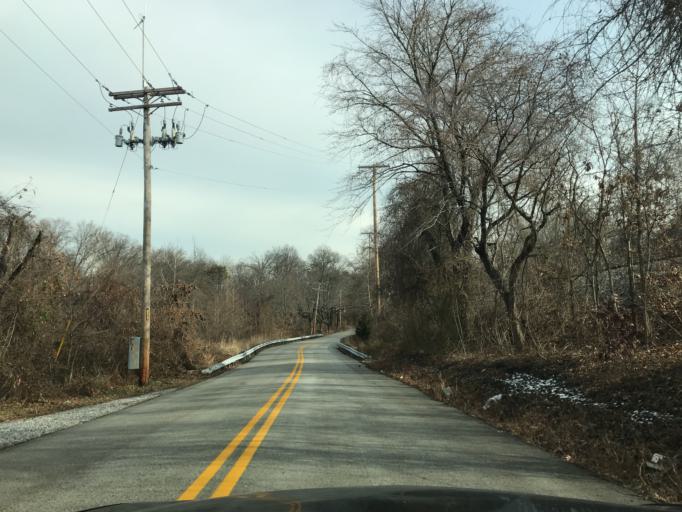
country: US
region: Maryland
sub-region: Howard County
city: Hanover
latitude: 39.1926
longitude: -76.7317
